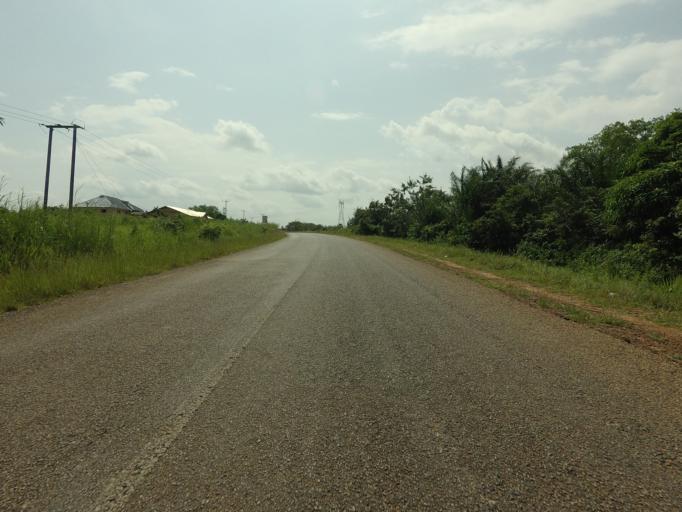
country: TG
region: Maritime
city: Lome
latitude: 6.2507
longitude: 0.9728
